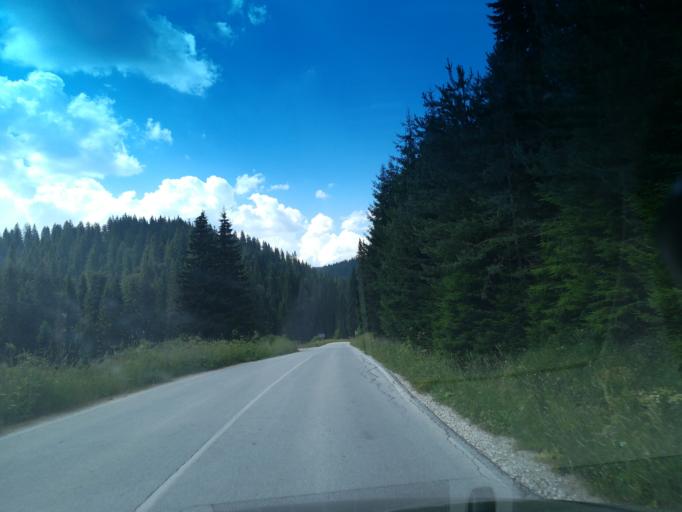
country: BG
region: Smolyan
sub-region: Obshtina Smolyan
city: Smolyan
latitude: 41.6569
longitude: 24.6848
